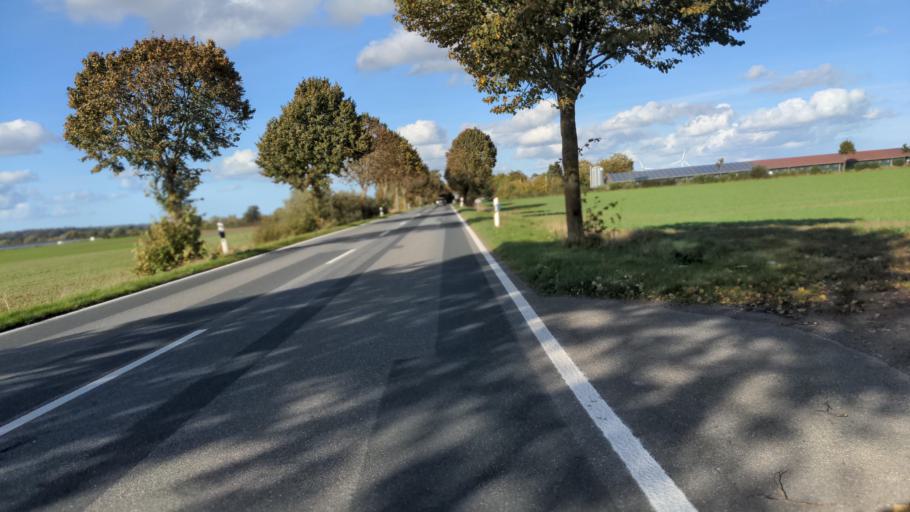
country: DE
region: Schleswig-Holstein
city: Beschendorf
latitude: 54.1704
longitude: 10.8739
